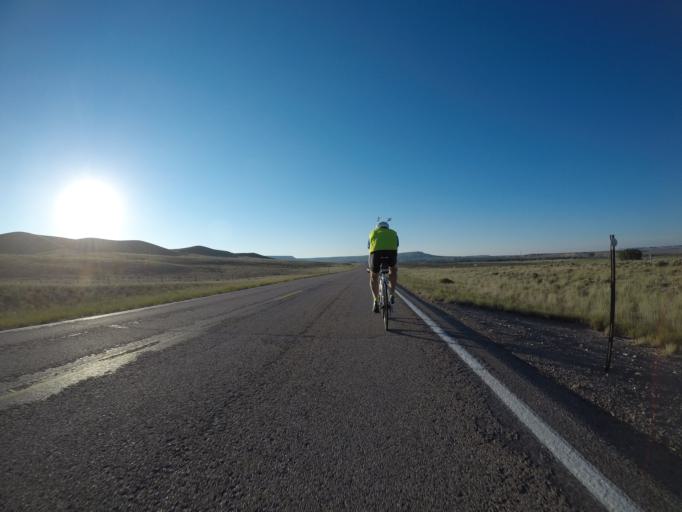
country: US
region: Wyoming
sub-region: Sublette County
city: Marbleton
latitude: 42.5758
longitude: -109.9826
